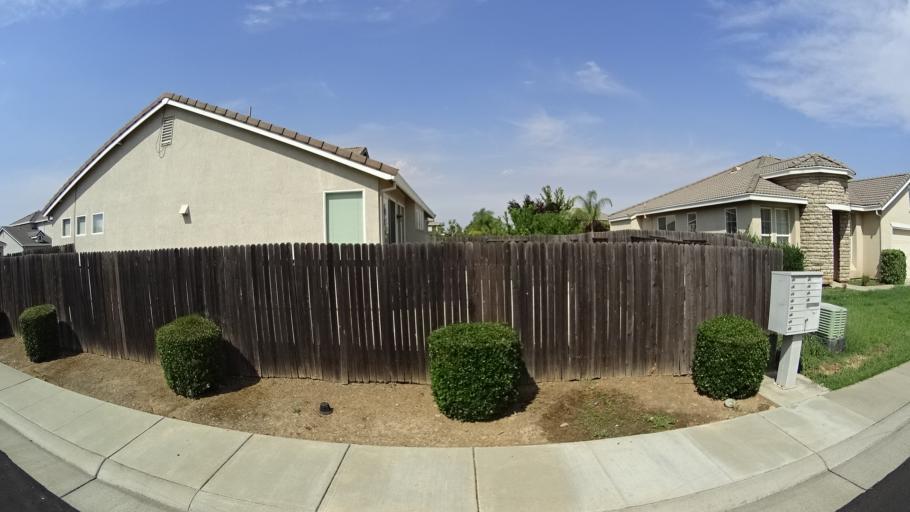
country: US
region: California
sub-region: Sacramento County
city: Laguna
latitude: 38.3872
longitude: -121.4458
